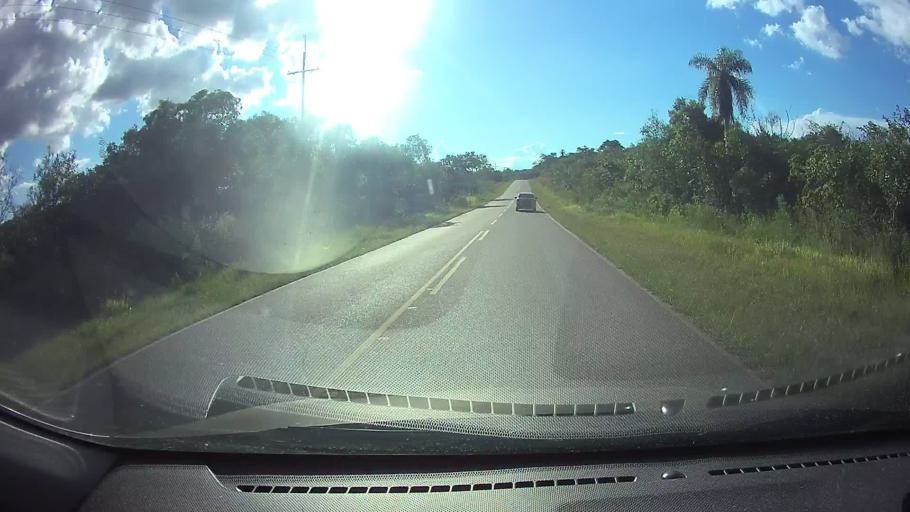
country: PY
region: Cordillera
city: Altos
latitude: -25.2793
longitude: -57.2151
